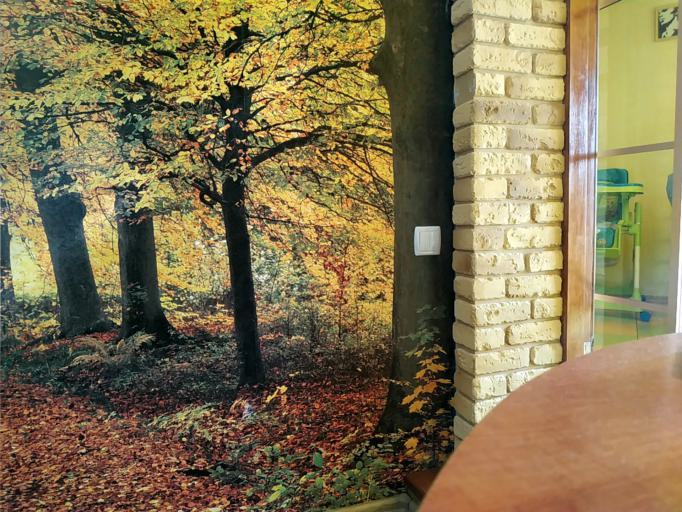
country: RU
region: Novgorod
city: Parfino
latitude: 57.8065
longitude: 31.5882
